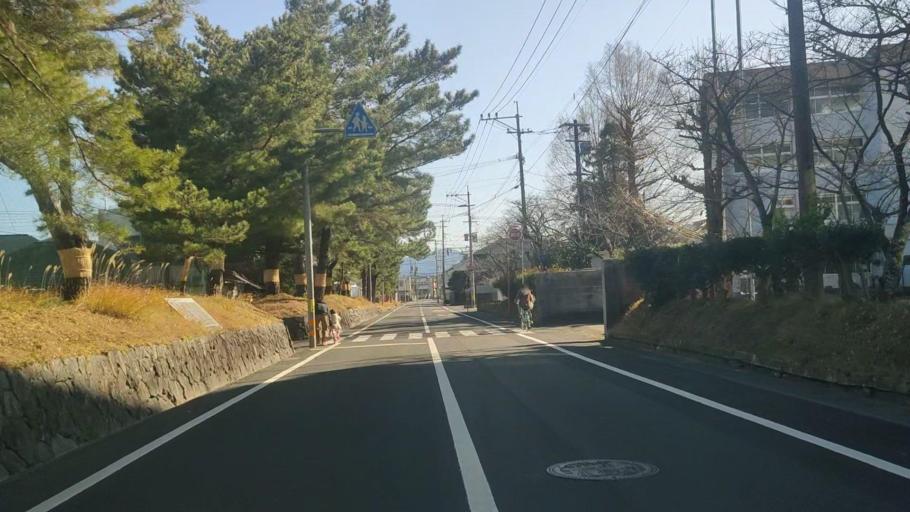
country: JP
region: Oita
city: Saiki
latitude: 32.9614
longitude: 131.8954
